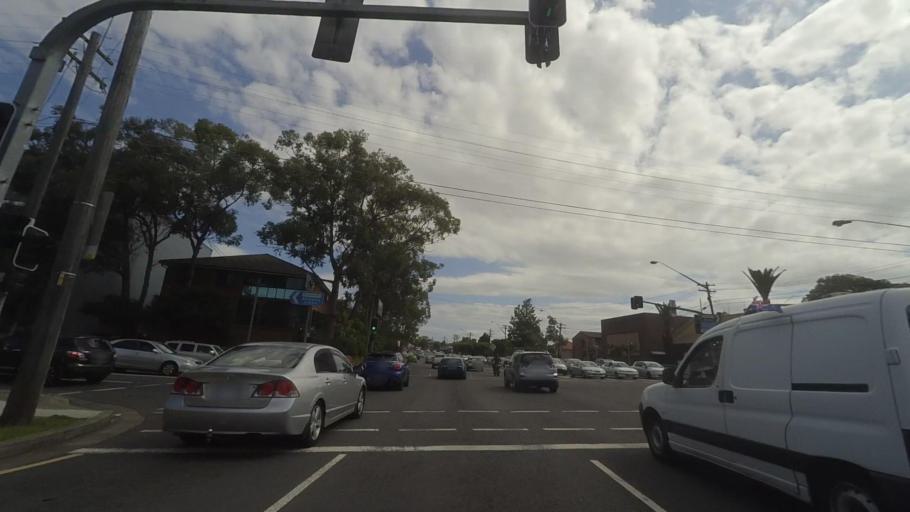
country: AU
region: New South Wales
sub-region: Auburn
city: Lidcombe
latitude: -33.8649
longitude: 151.0419
